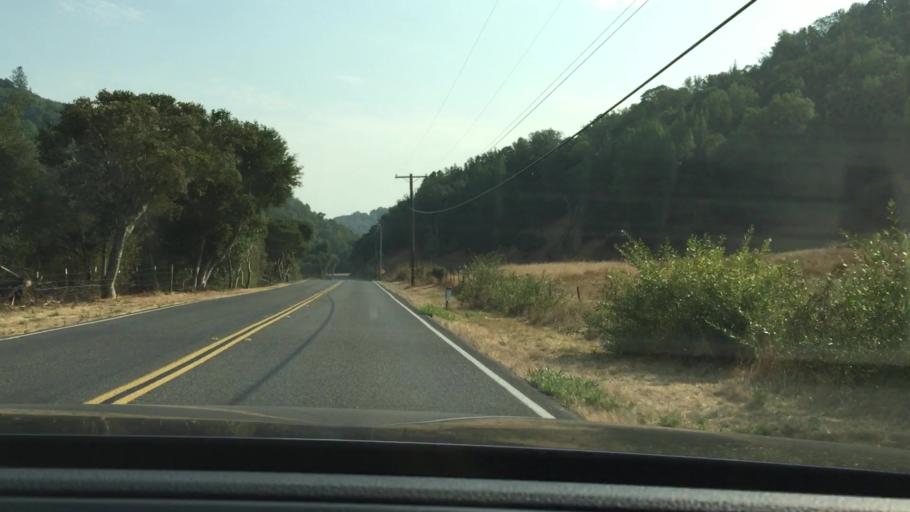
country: US
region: California
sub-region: Marin County
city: Lagunitas-Forest Knolls
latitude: 38.1306
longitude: -122.7131
